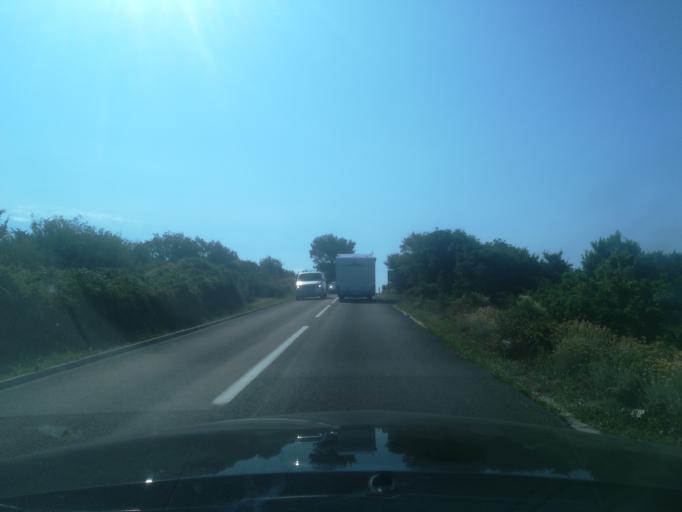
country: HR
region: Primorsko-Goranska
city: Banjol
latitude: 44.7237
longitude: 14.8200
